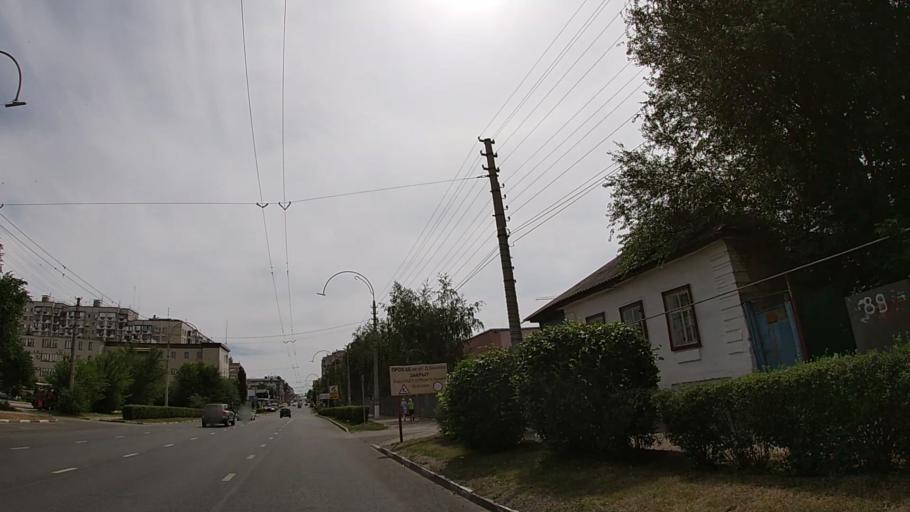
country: RU
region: Belgorod
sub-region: Belgorodskiy Rayon
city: Belgorod
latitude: 50.5993
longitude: 36.5753
